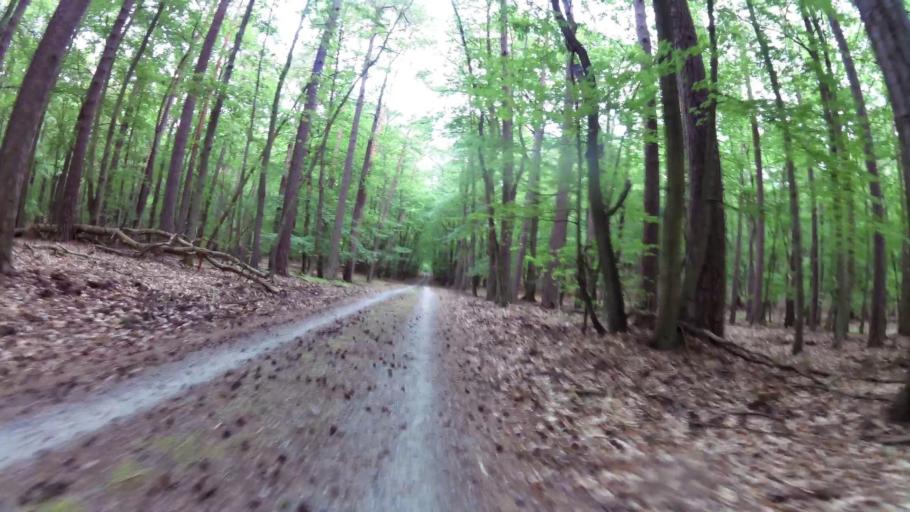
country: PL
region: West Pomeranian Voivodeship
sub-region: Powiat kamienski
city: Miedzyzdroje
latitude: 53.9387
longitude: 14.4950
